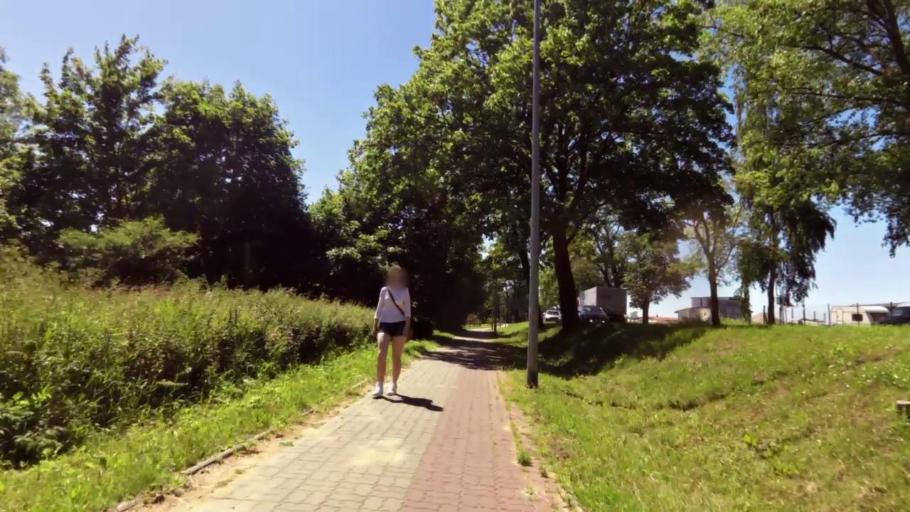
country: PL
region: West Pomeranian Voivodeship
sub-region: Powiat kolobrzeski
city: Kolobrzeg
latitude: 54.1531
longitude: 15.5637
